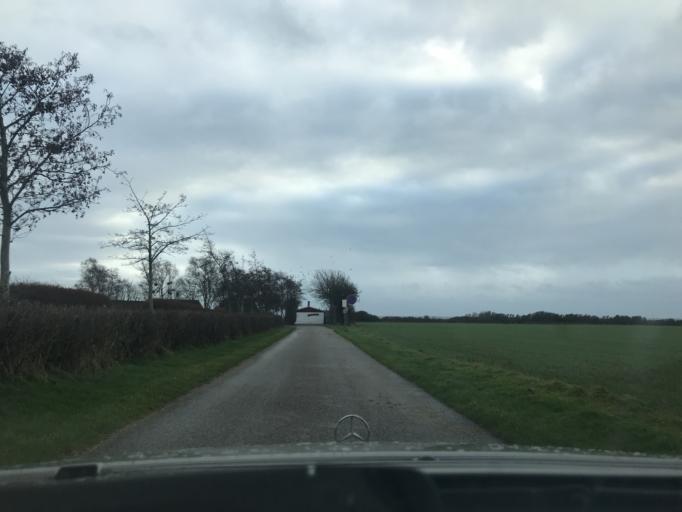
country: DK
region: South Denmark
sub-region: Sonderborg Kommune
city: Horuphav
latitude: 54.8723
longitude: 10.0128
